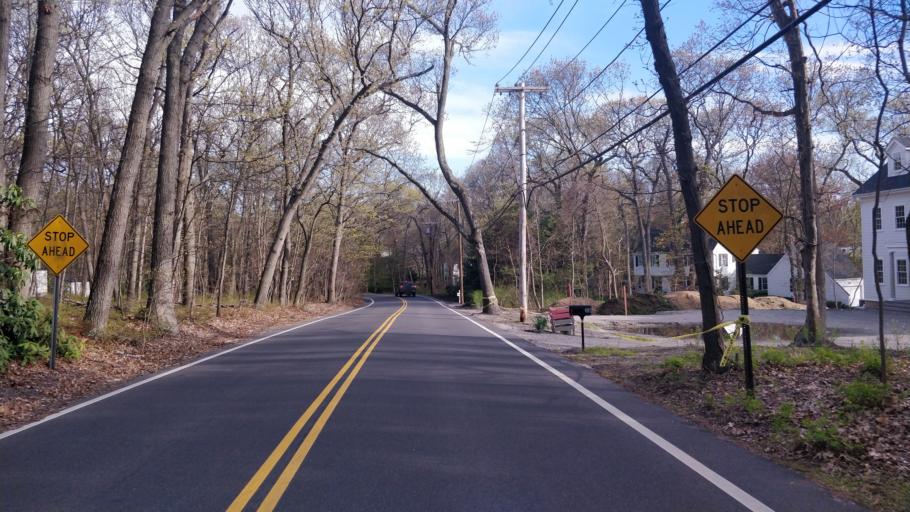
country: US
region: New York
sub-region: Suffolk County
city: Stony Brook
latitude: 40.9448
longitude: -73.1368
